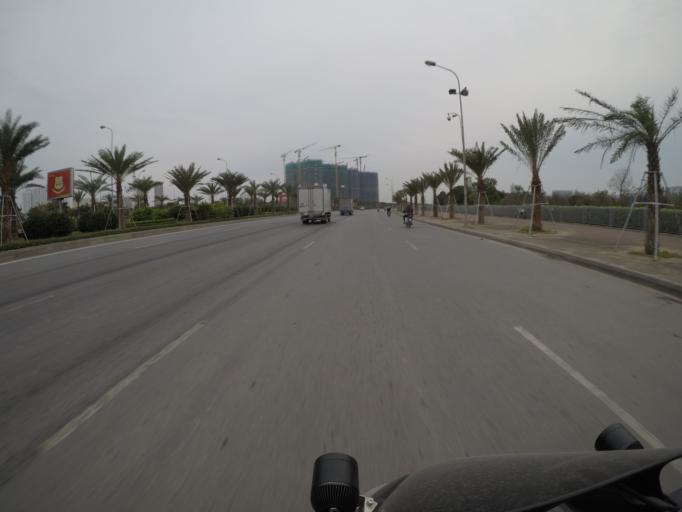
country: VN
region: Ha Noi
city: Thanh Xuan
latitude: 21.0031
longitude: 105.7883
